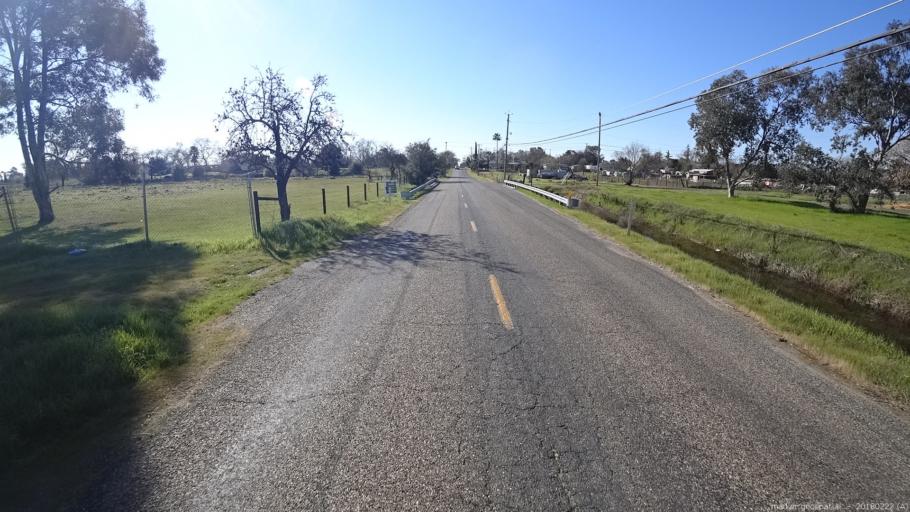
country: US
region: California
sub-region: Sacramento County
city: Elverta
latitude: 38.7165
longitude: -121.4512
